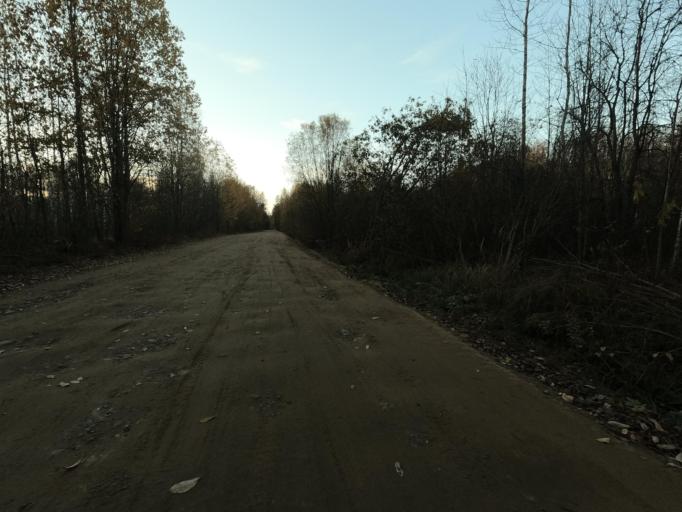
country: RU
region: Leningrad
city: Mga
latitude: 59.7566
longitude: 31.2746
